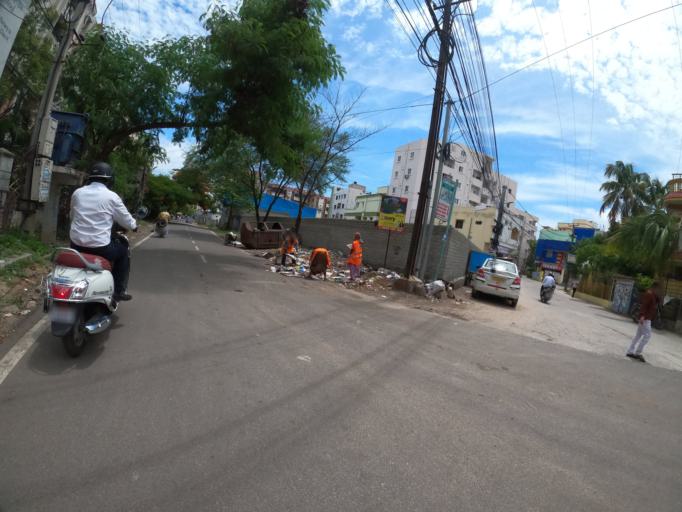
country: IN
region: Telangana
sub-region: Hyderabad
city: Hyderabad
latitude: 17.3664
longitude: 78.4224
